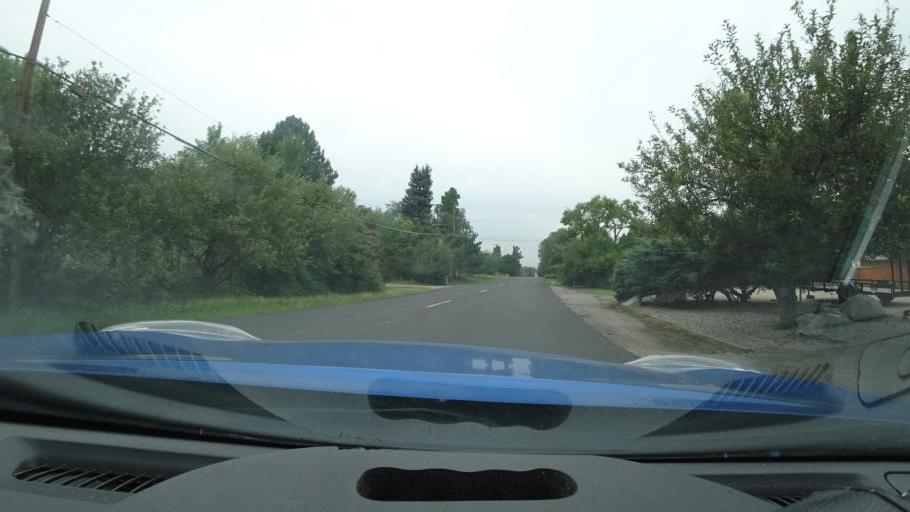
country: US
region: Colorado
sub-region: Arapahoe County
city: Glendale
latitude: 39.6821
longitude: -104.9084
